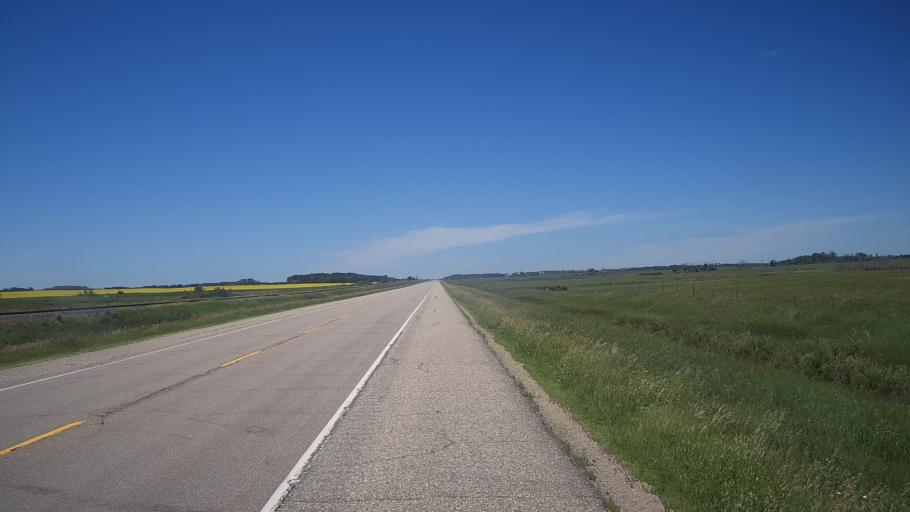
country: CA
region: Manitoba
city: Rivers
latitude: 50.4211
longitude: -100.4916
